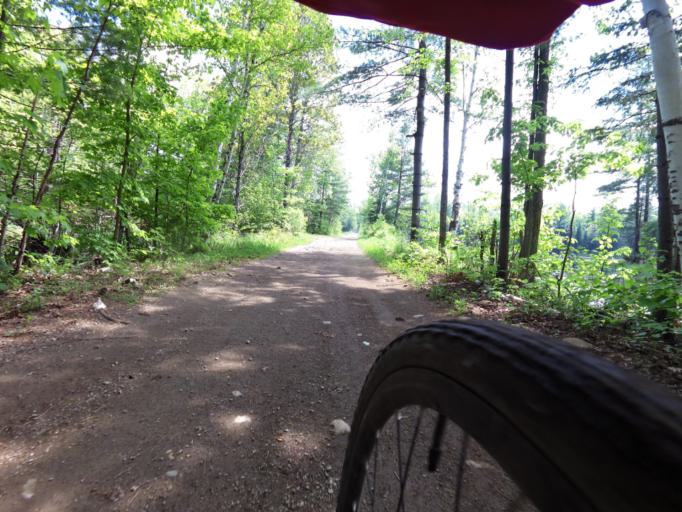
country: CA
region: Ontario
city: Renfrew
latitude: 45.2176
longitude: -76.6927
